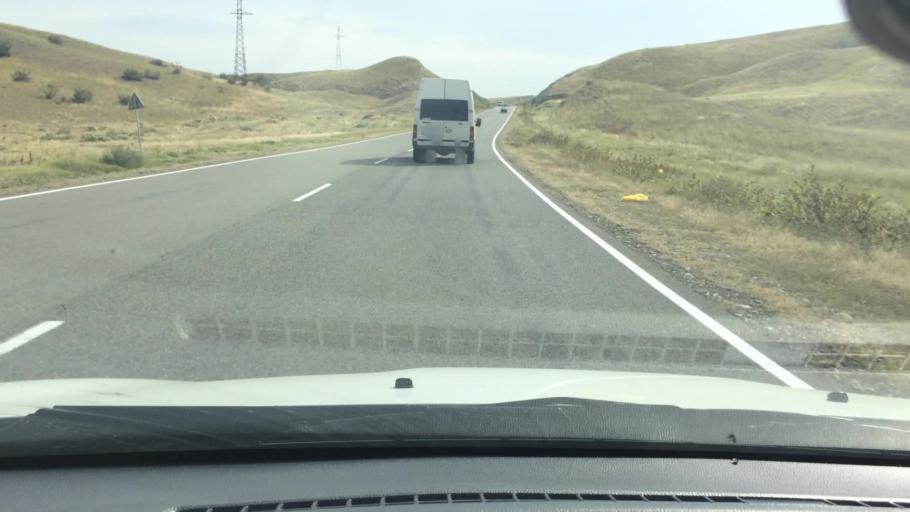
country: GE
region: Kvemo Kartli
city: Rust'avi
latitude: 41.5267
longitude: 44.9880
